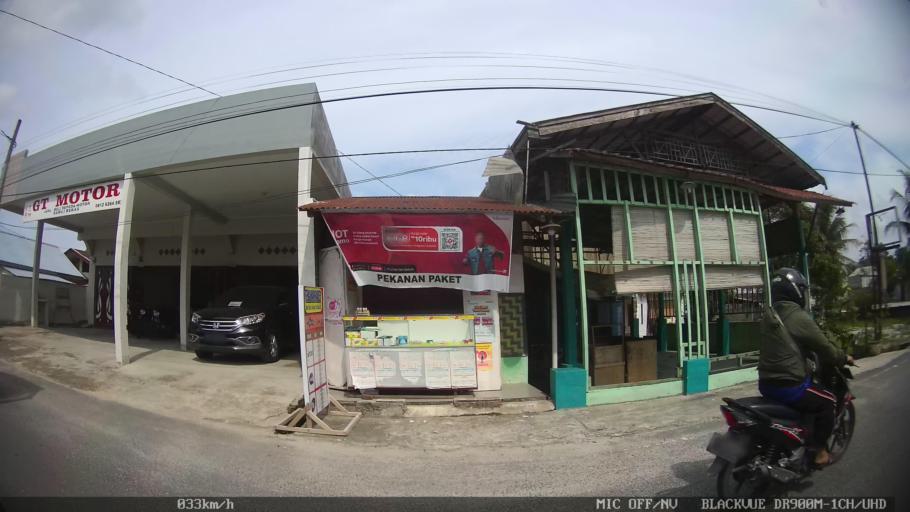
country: ID
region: North Sumatra
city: Percut
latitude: 3.5960
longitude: 98.8600
